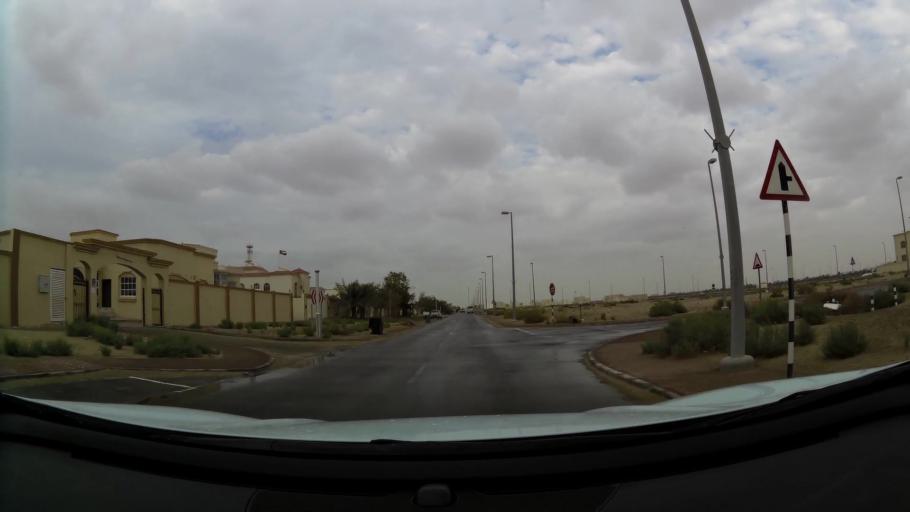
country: AE
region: Abu Dhabi
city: Abu Dhabi
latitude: 24.3559
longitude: 54.6378
